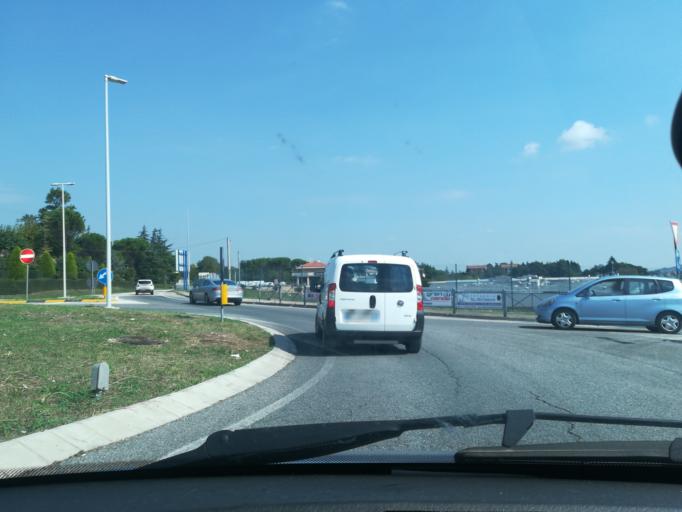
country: IT
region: The Marches
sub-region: Provincia di Macerata
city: Tolentino
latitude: 43.2171
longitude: 13.3112
